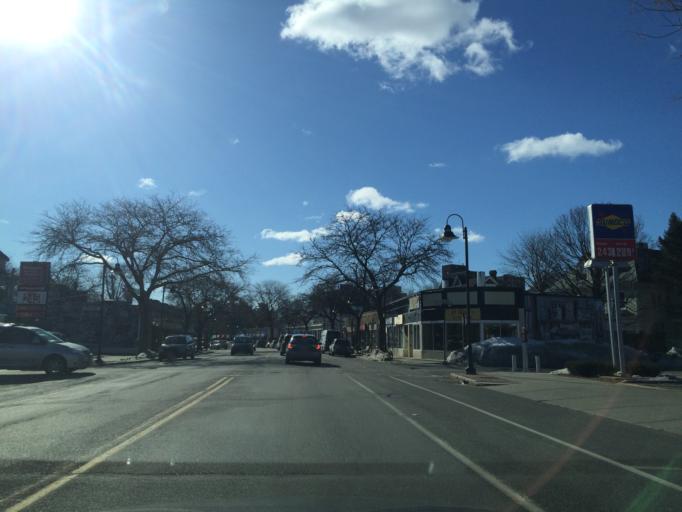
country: US
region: Massachusetts
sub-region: Norfolk County
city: Brookline
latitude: 42.3467
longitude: -71.1284
